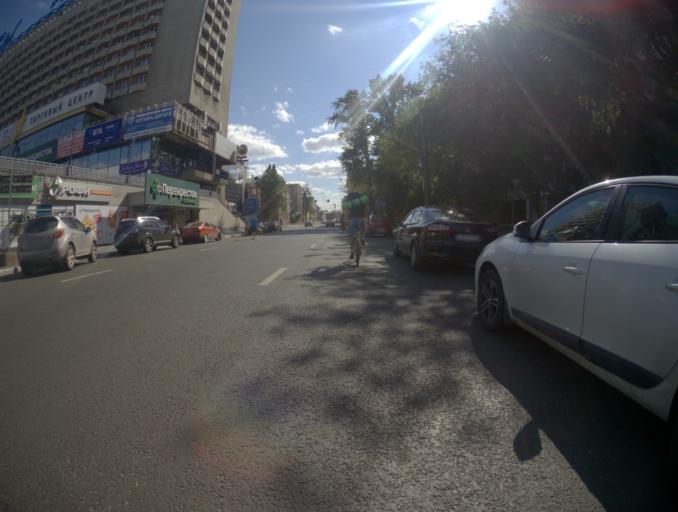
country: RU
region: Nizjnij Novgorod
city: Nizhniy Novgorod
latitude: 56.3262
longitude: 43.9576
